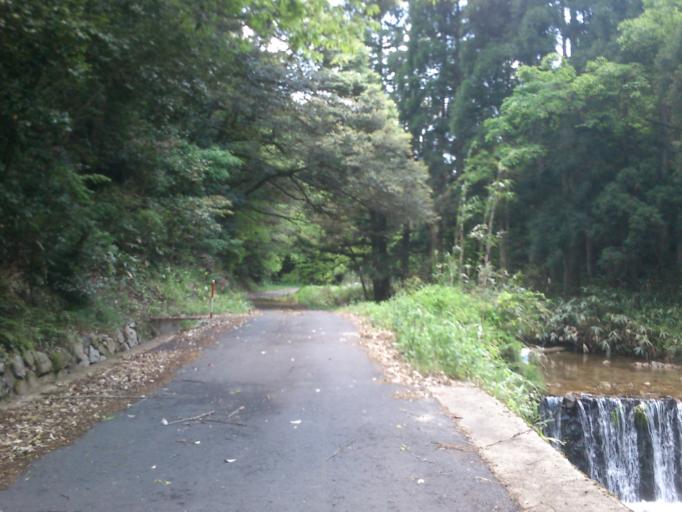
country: JP
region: Kyoto
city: Miyazu
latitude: 35.7055
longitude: 135.1186
